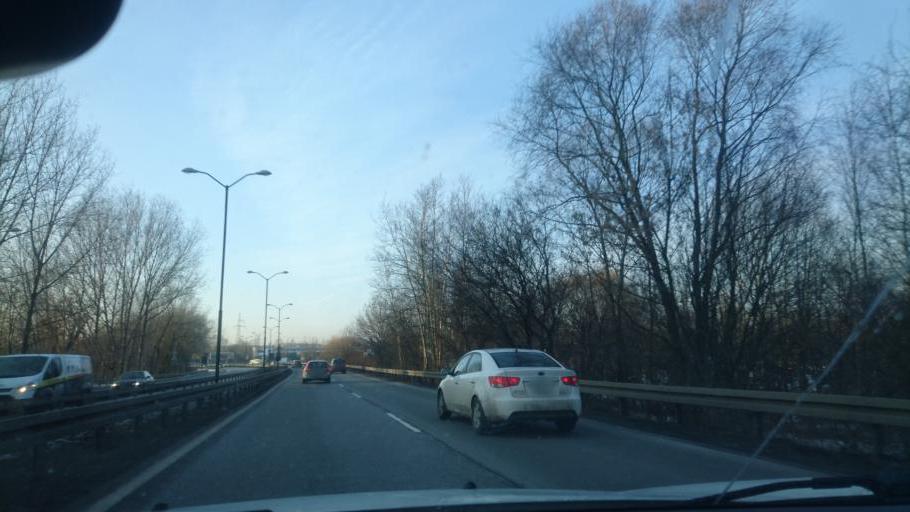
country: PL
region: Silesian Voivodeship
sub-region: Katowice
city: Katowice
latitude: 50.2617
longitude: 19.0630
